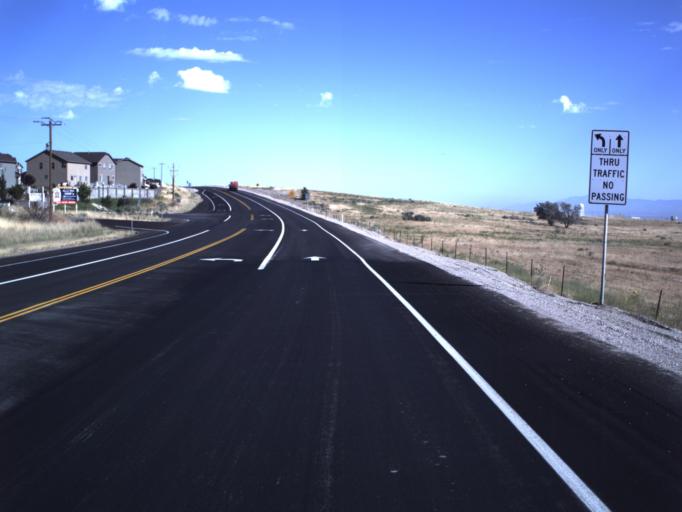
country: US
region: Utah
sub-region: Salt Lake County
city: Oquirrh
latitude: 40.6299
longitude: -112.0529
